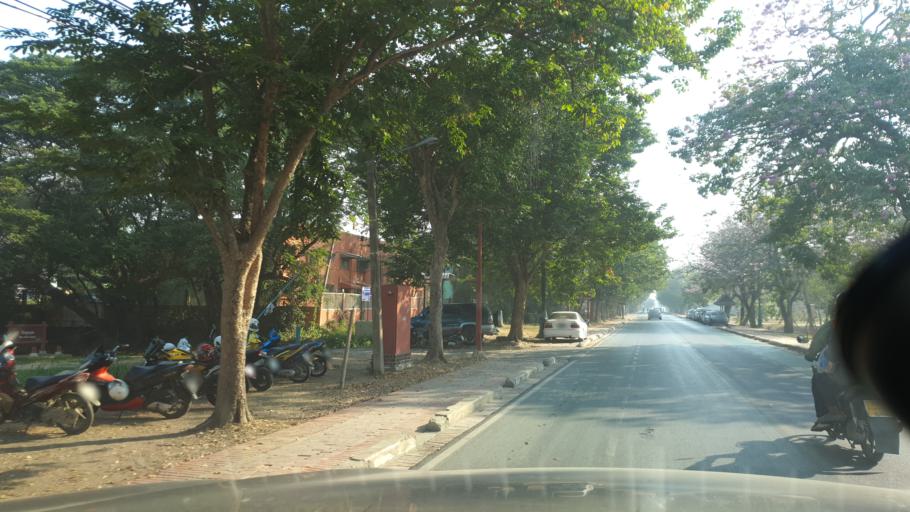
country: TH
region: Phra Nakhon Si Ayutthaya
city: Phra Nakhon Si Ayutthaya
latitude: 14.3576
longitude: 100.5647
